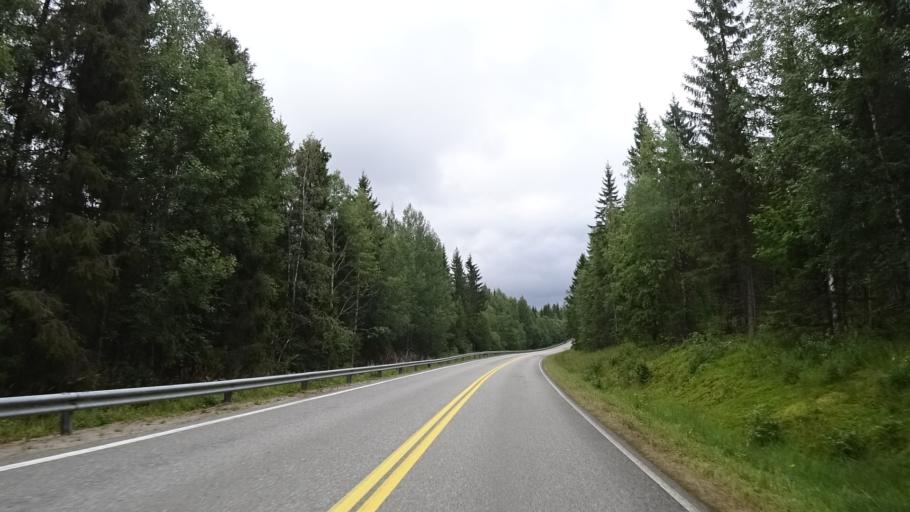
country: FI
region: North Karelia
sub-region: Joensuu
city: Ilomantsi
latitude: 63.2615
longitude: 30.6823
